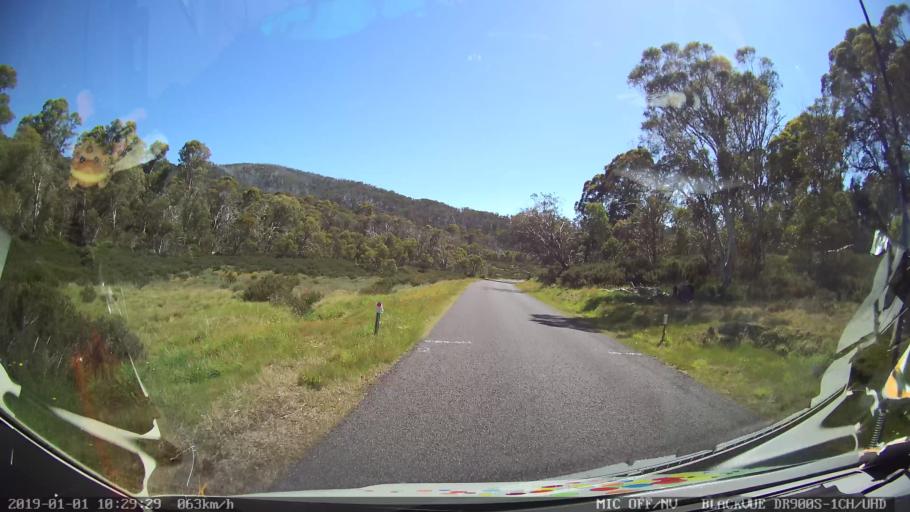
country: AU
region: New South Wales
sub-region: Snowy River
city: Jindabyne
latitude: -36.0540
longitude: 148.2478
